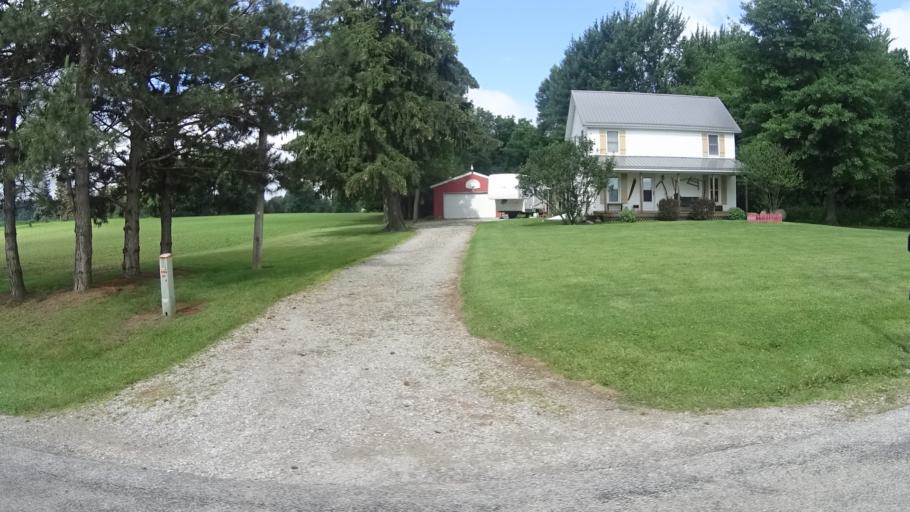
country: US
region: Ohio
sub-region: Huron County
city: Wakeman
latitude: 41.2967
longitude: -82.4428
